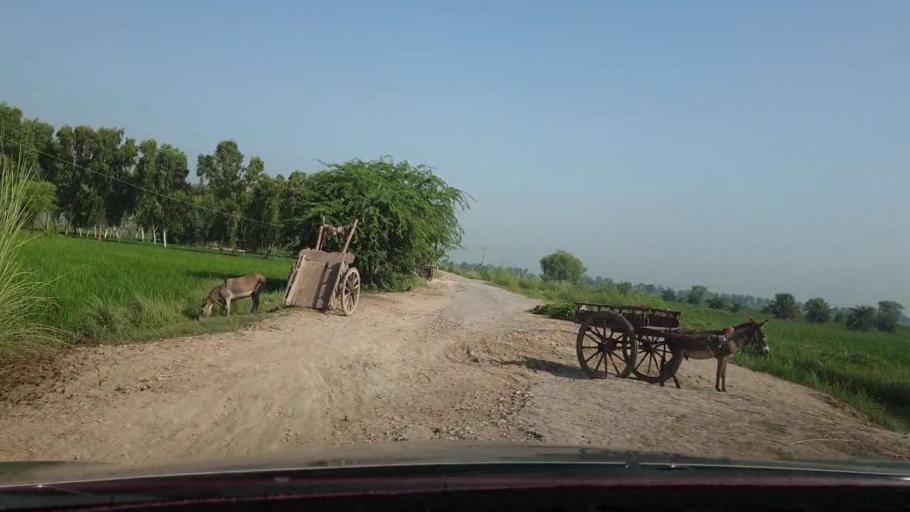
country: PK
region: Sindh
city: Nasirabad
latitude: 27.4408
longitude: 67.9206
